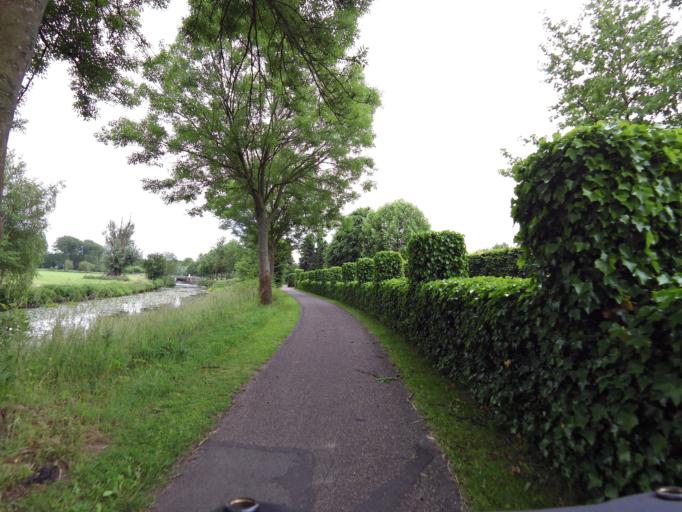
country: NL
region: North Brabant
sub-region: Gemeente Breda
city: Breda
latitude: 51.5007
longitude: 4.7803
